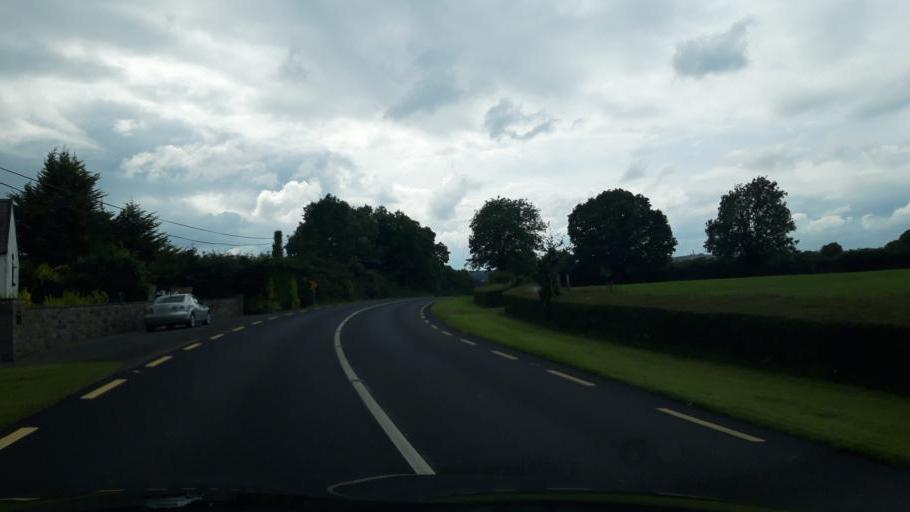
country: IE
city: Ballylinan
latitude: 52.9098
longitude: -7.0798
